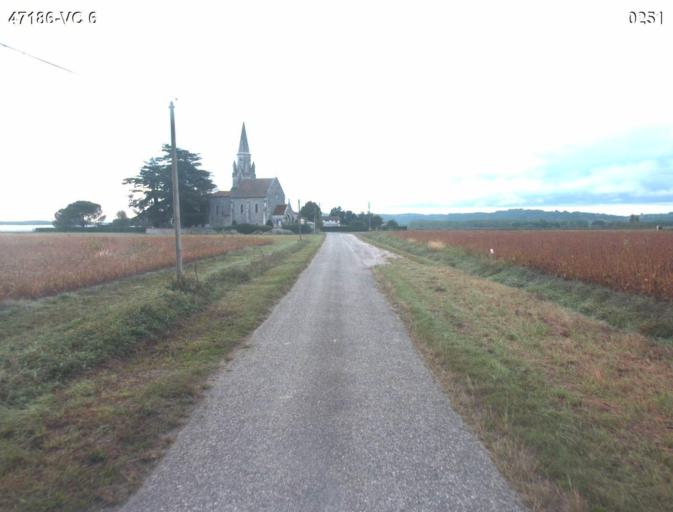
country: FR
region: Aquitaine
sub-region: Departement du Lot-et-Garonne
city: Port-Sainte-Marie
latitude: 44.2305
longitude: 0.4447
